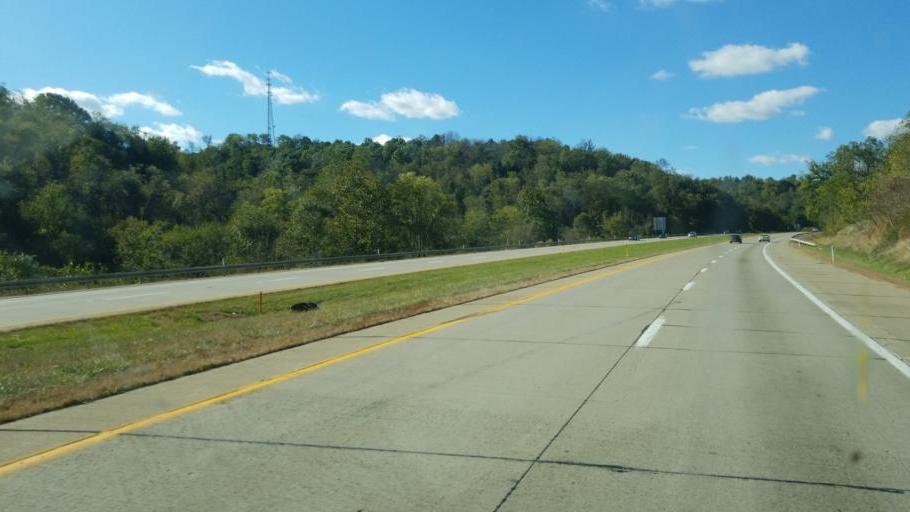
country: US
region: Pennsylvania
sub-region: Greene County
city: Morrisville
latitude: 39.9126
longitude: -80.1585
